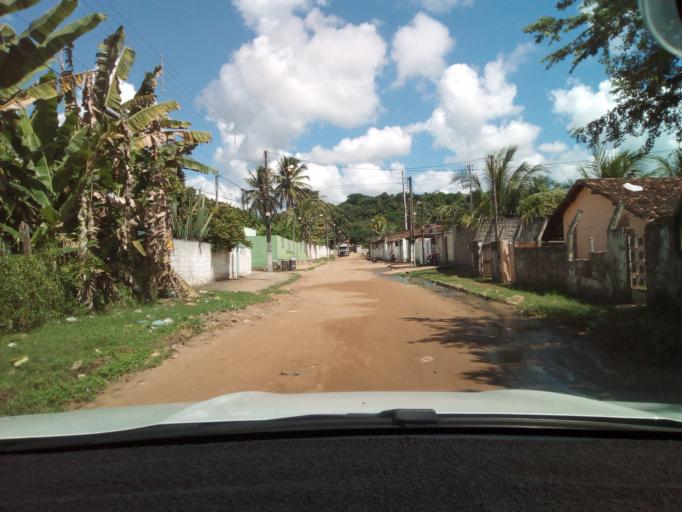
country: BR
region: Paraiba
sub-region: Bayeux
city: Bayeux
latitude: -7.1373
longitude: -34.9328
